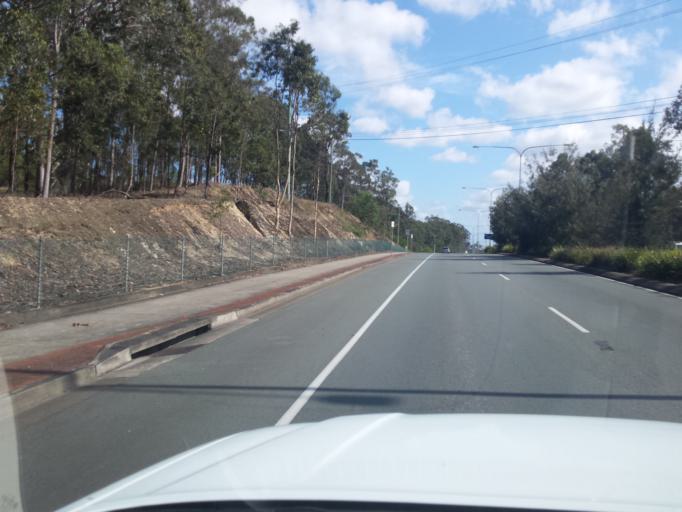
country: AU
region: Queensland
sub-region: Brisbane
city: Bridegman Downs
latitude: -27.3779
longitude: 152.9805
